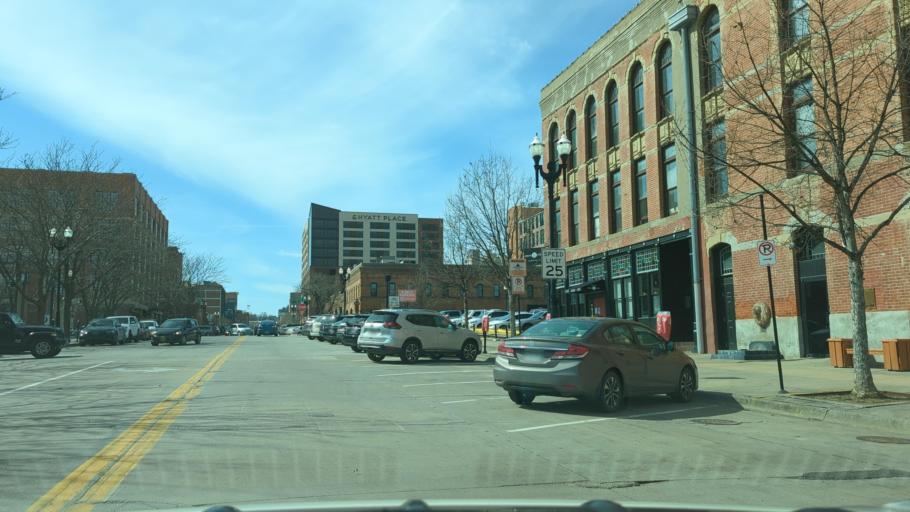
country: US
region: Nebraska
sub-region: Douglas County
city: Omaha
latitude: 41.2544
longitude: -95.9294
